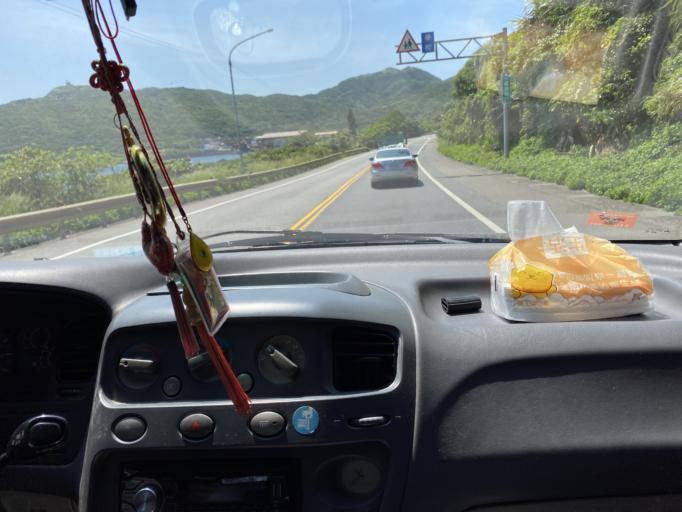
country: TW
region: Taiwan
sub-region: Keelung
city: Keelung
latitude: 25.0182
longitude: 121.9882
